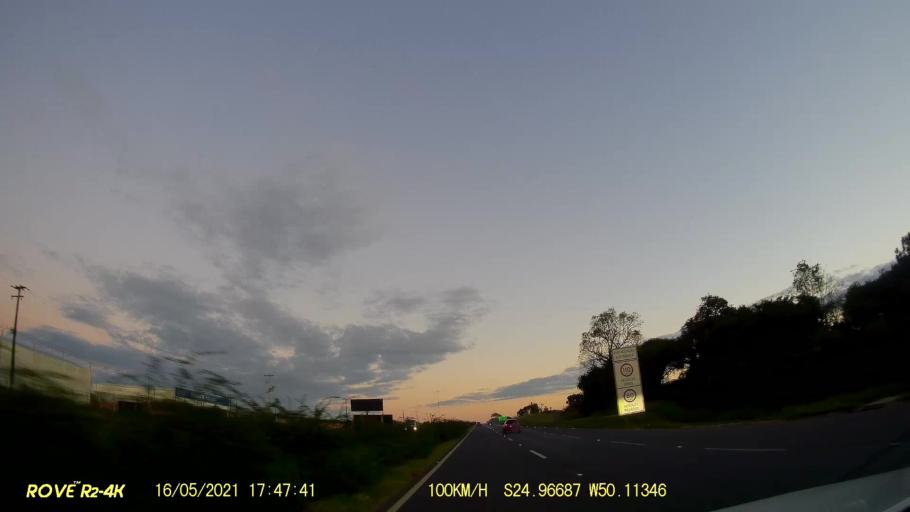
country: BR
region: Parana
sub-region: Carambei
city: Carambei
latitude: -24.9671
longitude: -50.1134
